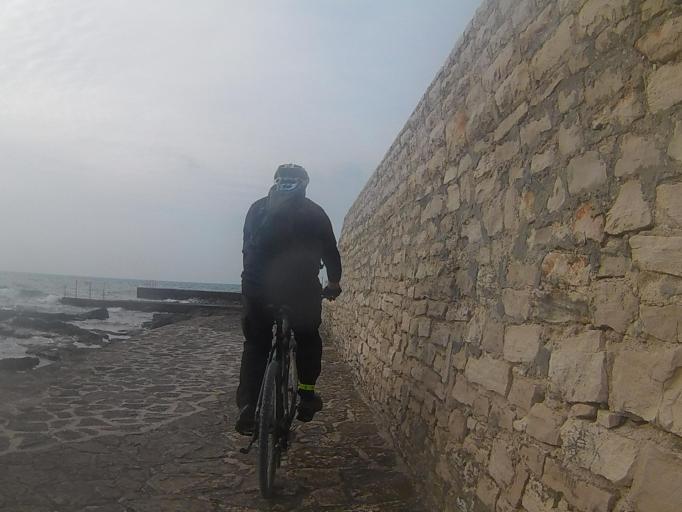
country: HR
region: Istarska
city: Novigrad
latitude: 45.3153
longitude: 13.5581
